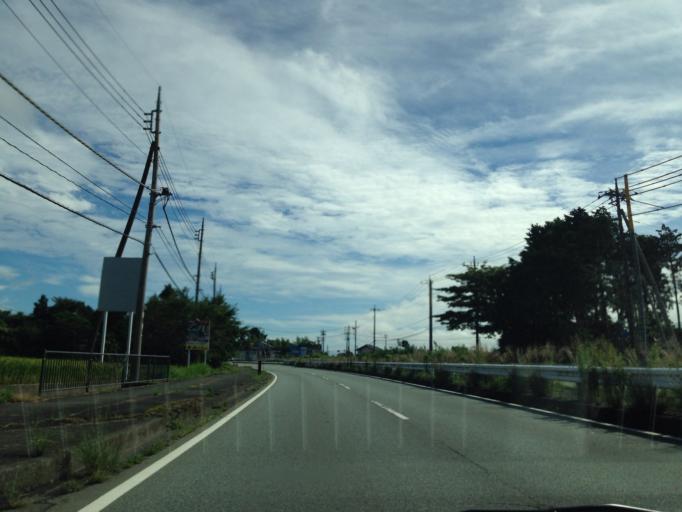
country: JP
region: Shizuoka
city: Gotemba
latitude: 35.2775
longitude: 138.9167
